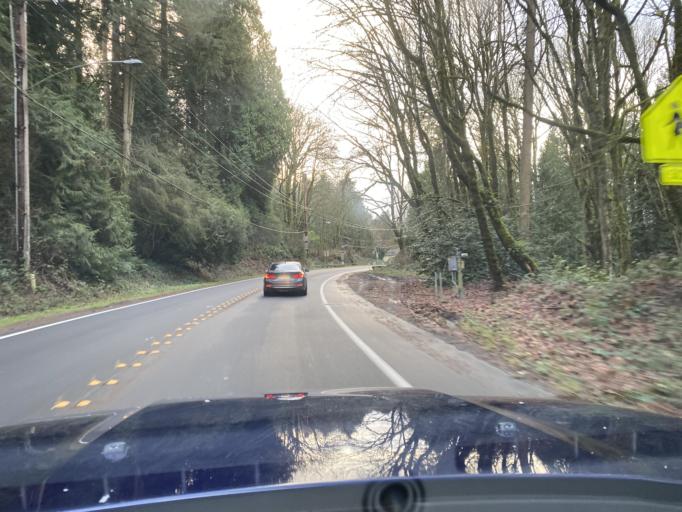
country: US
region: Washington
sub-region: King County
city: Eastgate
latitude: 47.5705
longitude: -122.1329
